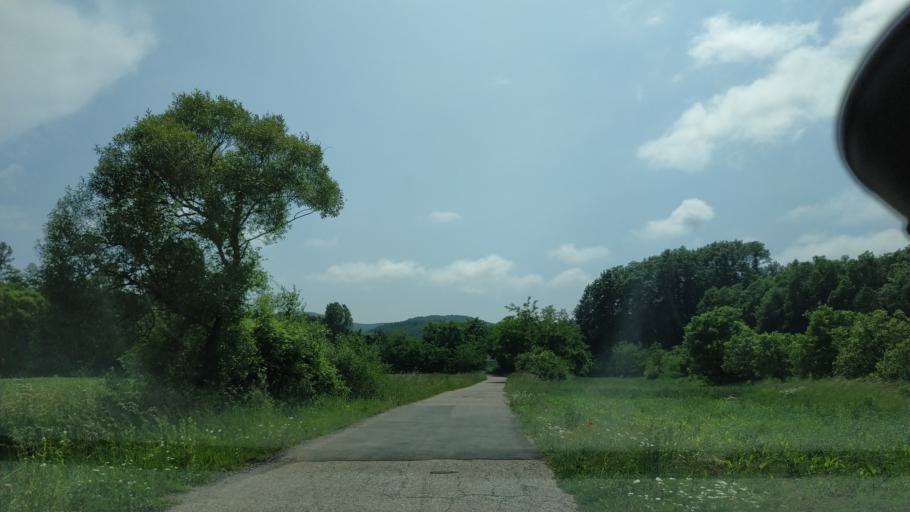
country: RS
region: Central Serbia
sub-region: Nisavski Okrug
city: Aleksinac
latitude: 43.4232
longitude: 21.7191
